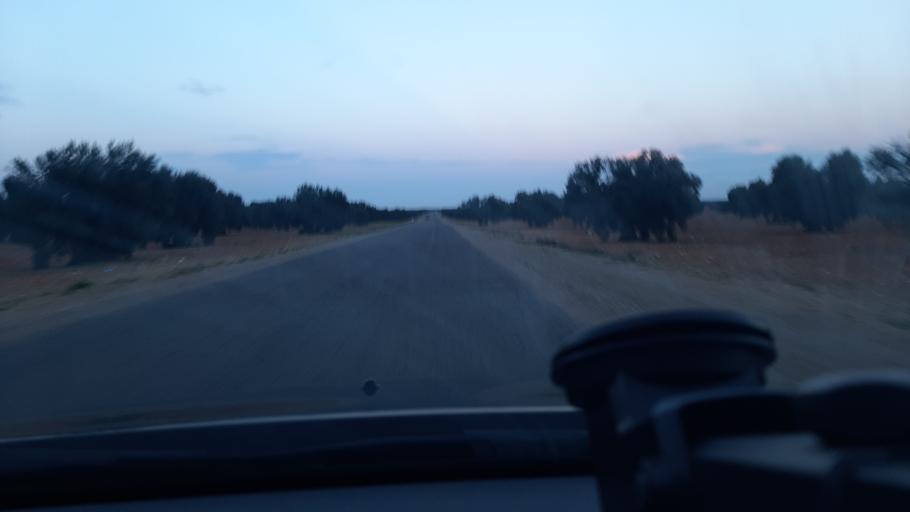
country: TN
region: Al Mahdiyah
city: Shurban
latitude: 34.9926
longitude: 10.3998
